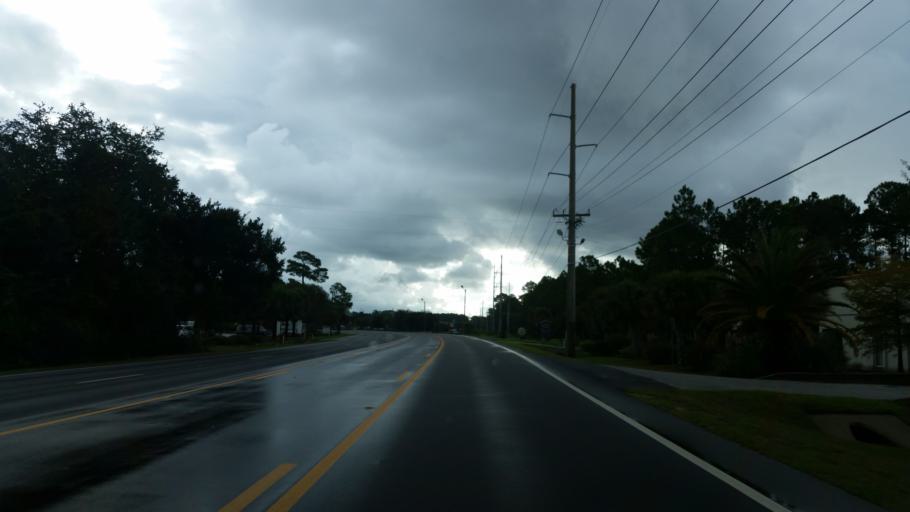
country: US
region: Alabama
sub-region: Baldwin County
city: Orange Beach
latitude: 30.2903
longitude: -87.5889
